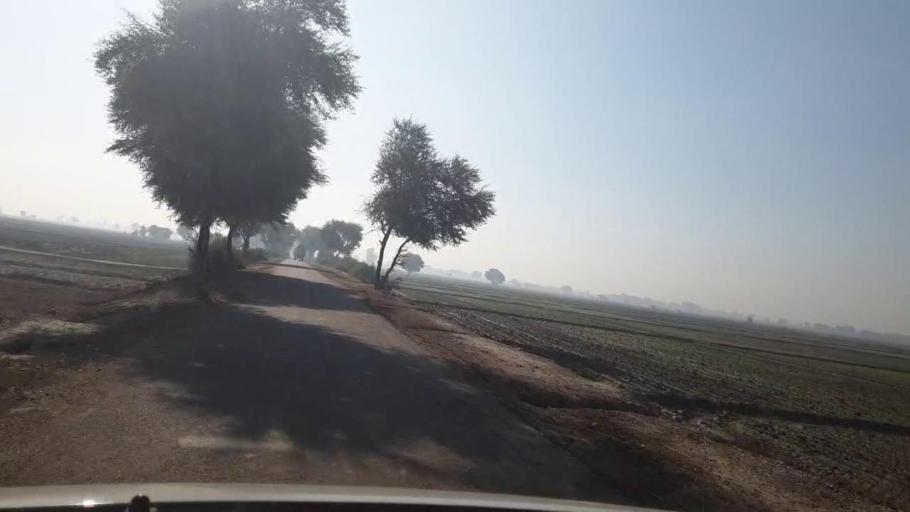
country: PK
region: Sindh
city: Dadu
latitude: 26.6677
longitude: 67.8161
